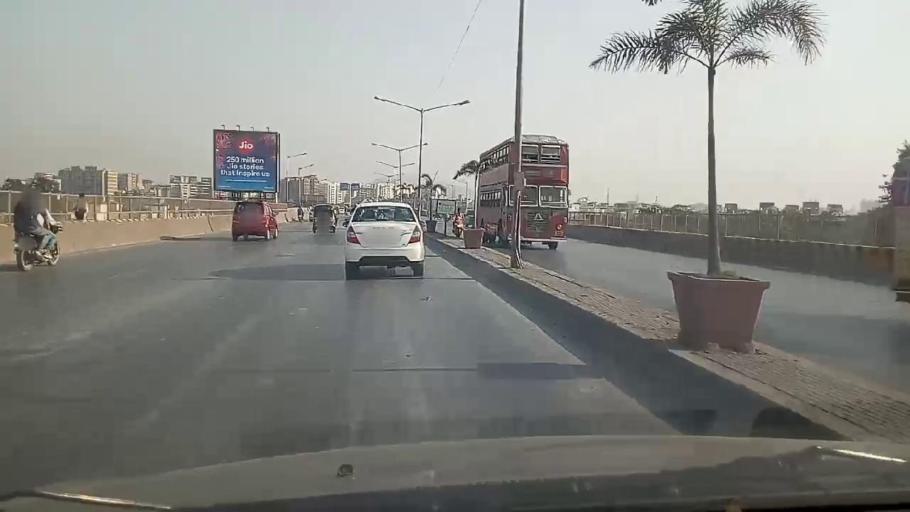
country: IN
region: Maharashtra
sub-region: Mumbai Suburban
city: Mumbai
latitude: 19.0710
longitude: 72.8858
